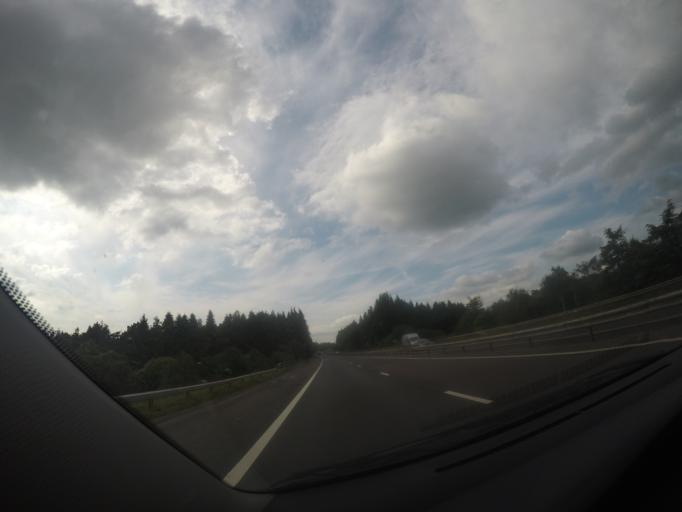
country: GB
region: Scotland
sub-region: South Lanarkshire
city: Douglas
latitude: 55.5779
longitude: -3.8170
